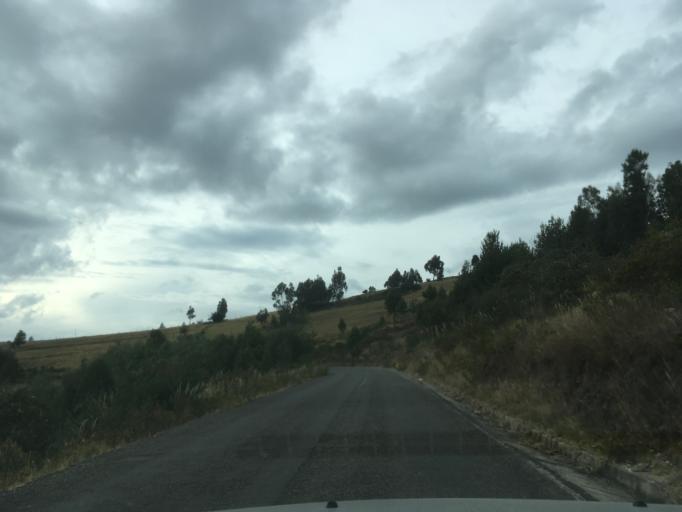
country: CO
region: Boyaca
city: Firavitoba
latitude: 5.6813
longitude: -73.0302
